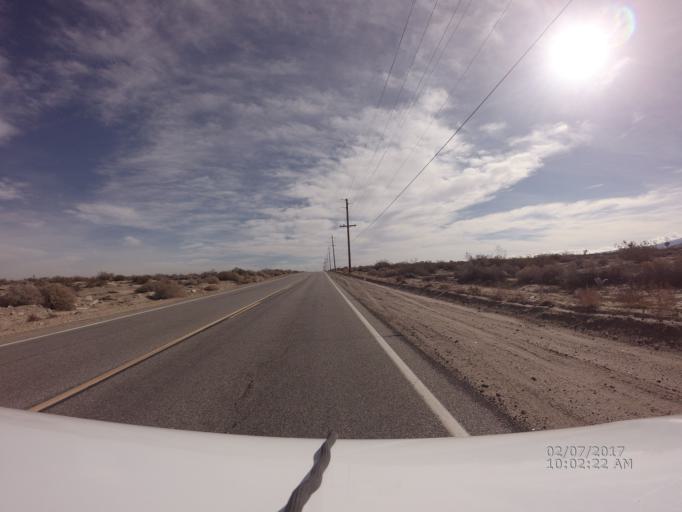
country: US
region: California
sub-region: Los Angeles County
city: Lake Los Angeles
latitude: 34.5798
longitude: -117.7276
